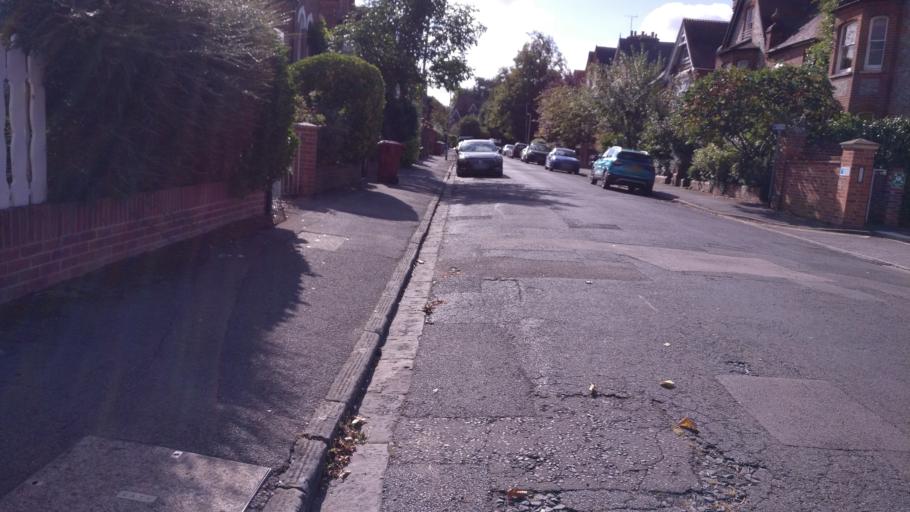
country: GB
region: England
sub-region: Reading
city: Reading
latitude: 51.4517
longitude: -0.9546
